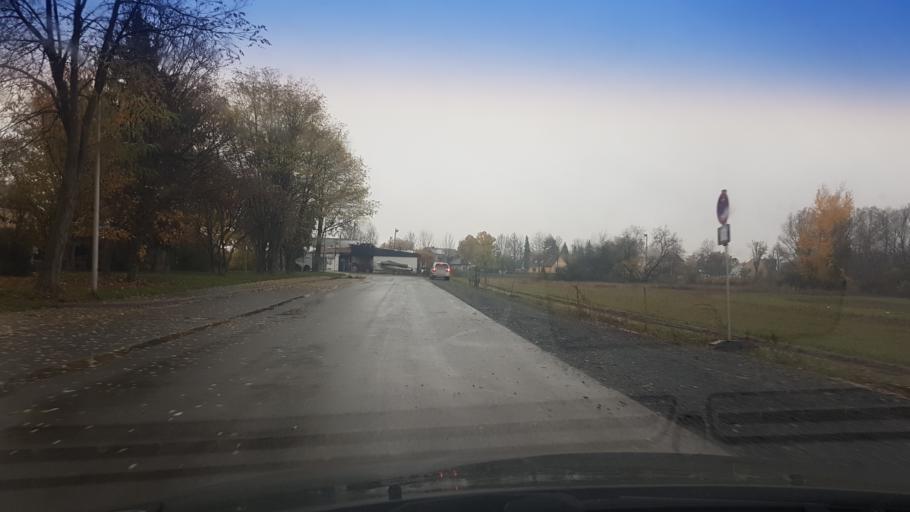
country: DE
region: Bavaria
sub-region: Upper Franconia
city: Baunach
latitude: 49.9913
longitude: 10.8523
